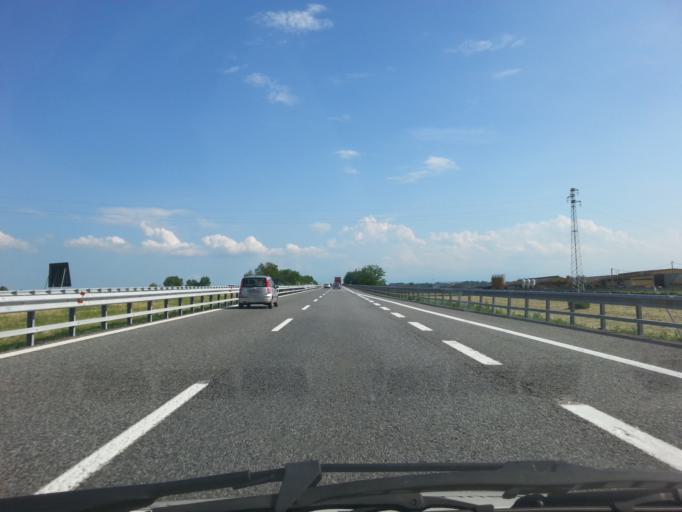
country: IT
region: Piedmont
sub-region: Provincia di Cuneo
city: Marene
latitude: 44.7016
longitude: 7.7637
